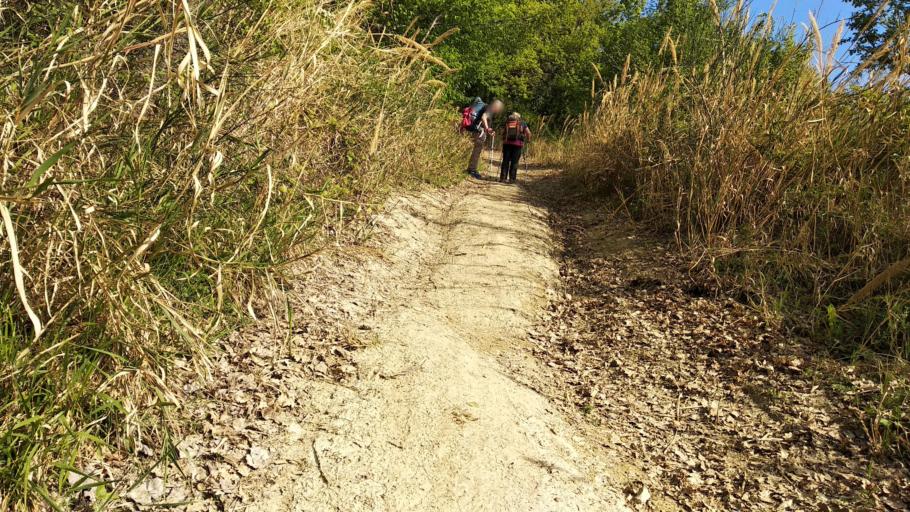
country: IT
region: Emilia-Romagna
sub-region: Provincia di Ravenna
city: Fognano
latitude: 44.2259
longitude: 11.7224
